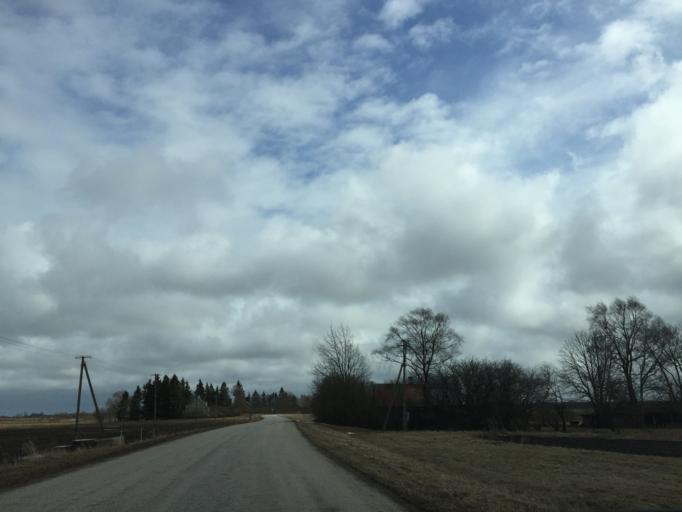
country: EE
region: Laeaene
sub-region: Lihula vald
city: Lihula
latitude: 58.7329
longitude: 23.8680
